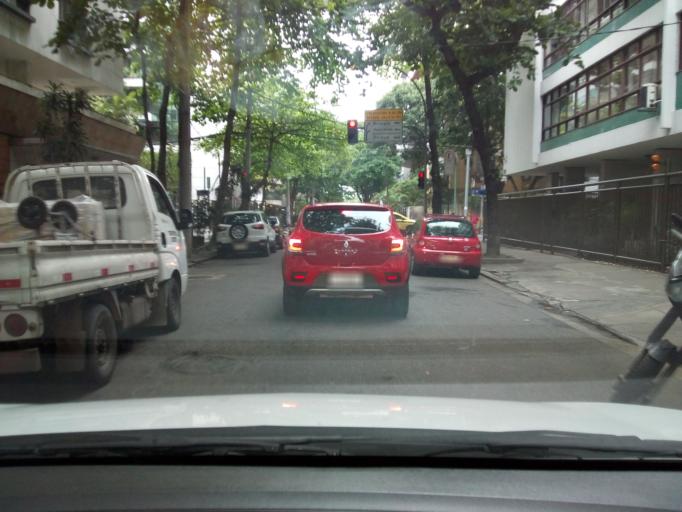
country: BR
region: Rio de Janeiro
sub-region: Rio De Janeiro
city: Rio de Janeiro
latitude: -22.9848
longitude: -43.2222
